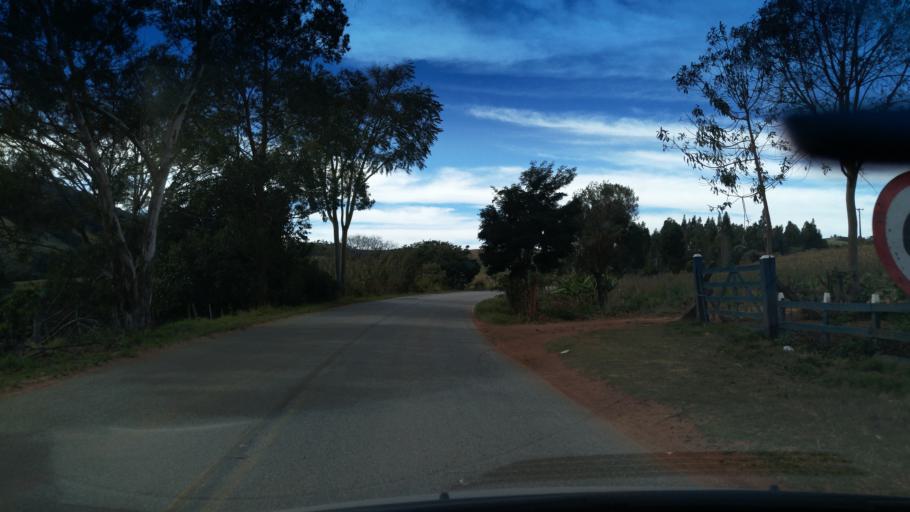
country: BR
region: Minas Gerais
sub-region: Andradas
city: Andradas
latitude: -22.0538
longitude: -46.4013
